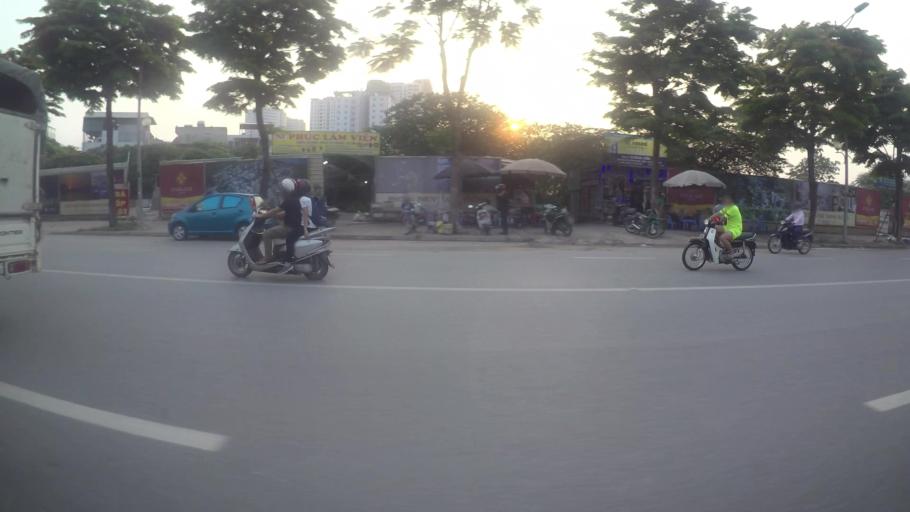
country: VN
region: Ha Noi
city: Tay Ho
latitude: 21.0519
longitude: 105.8043
